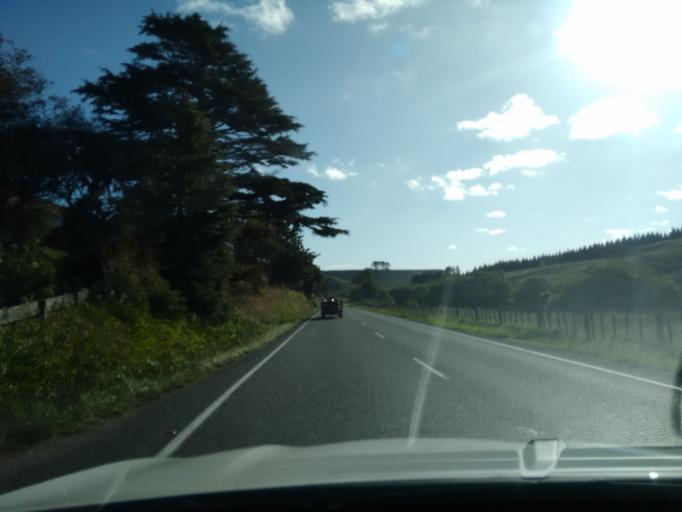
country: NZ
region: Manawatu-Wanganui
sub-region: Wanganui District
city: Wanganui
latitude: -39.8544
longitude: 174.9456
